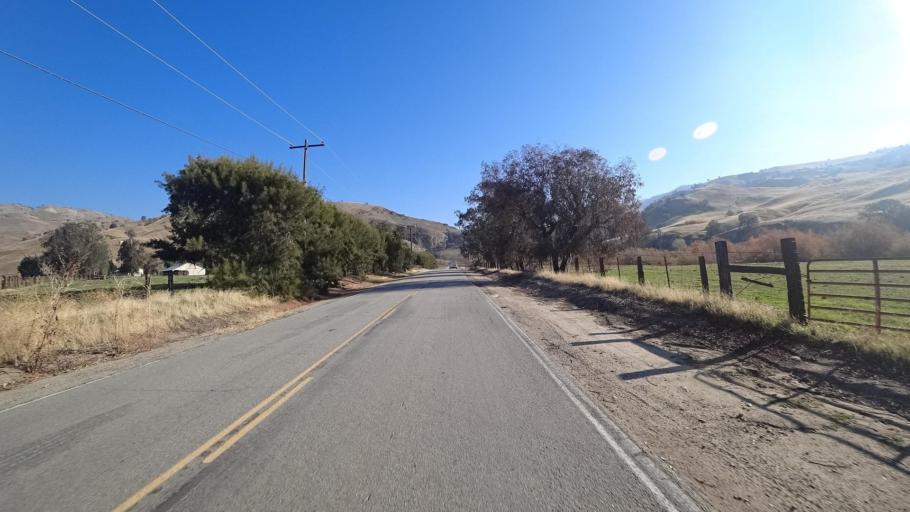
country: US
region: California
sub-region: Kern County
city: Bear Valley Springs
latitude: 35.2950
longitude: -118.6140
